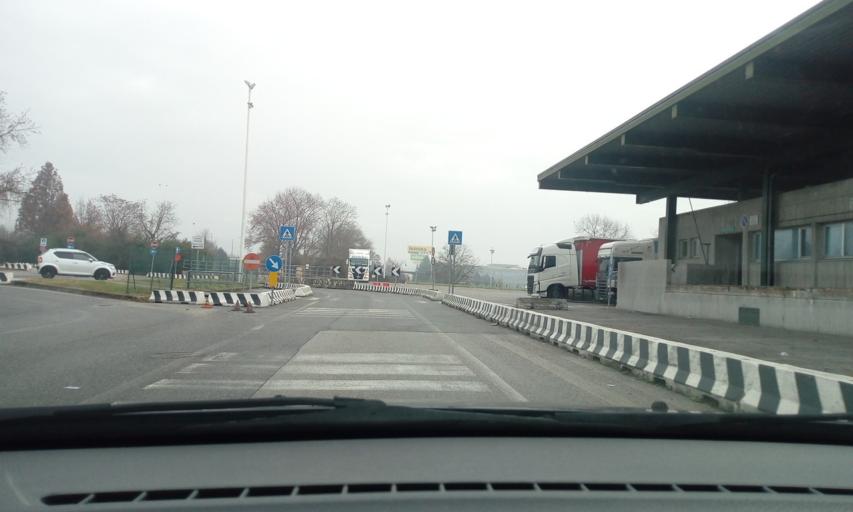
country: SI
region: Sempeter-Vrtojba
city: Vrtojba
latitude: 45.9185
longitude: 13.6188
